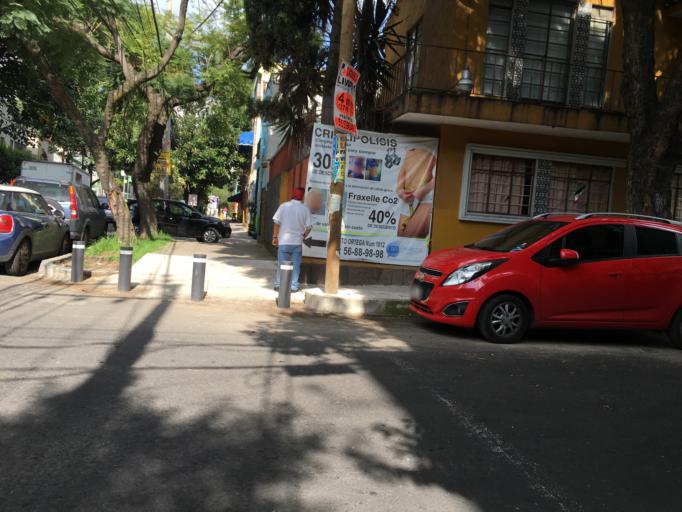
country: MX
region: Mexico City
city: Colonia del Valle
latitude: 19.3754
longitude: -99.1661
